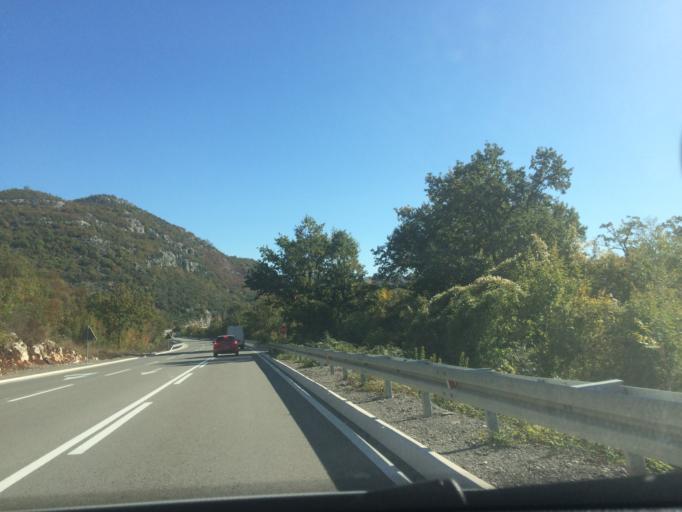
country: ME
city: Mojanovici
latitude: 42.3858
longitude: 19.0831
